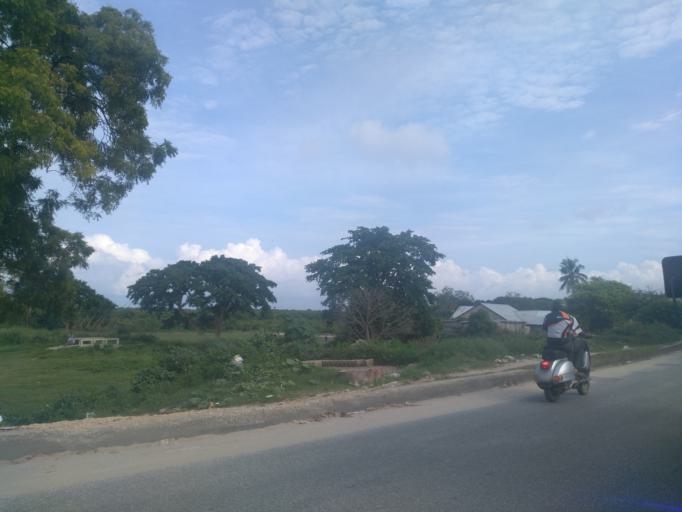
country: TZ
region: Zanzibar Urban/West
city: Zanzibar
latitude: -6.1528
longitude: 39.2091
